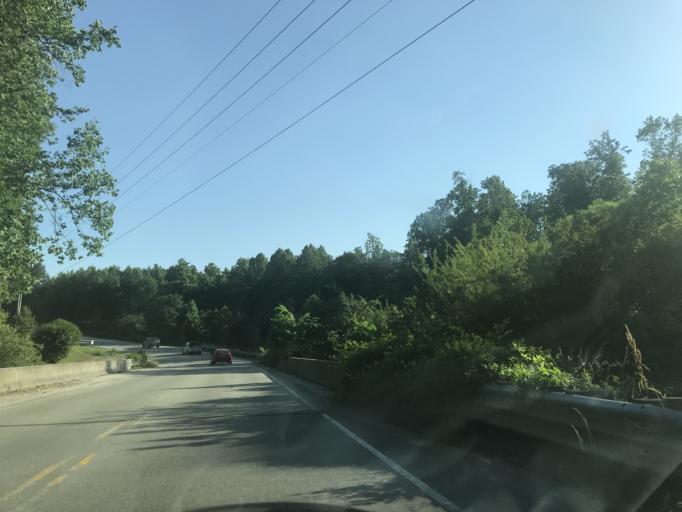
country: US
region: North Carolina
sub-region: Wake County
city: Garner
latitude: 35.7280
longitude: -78.6002
